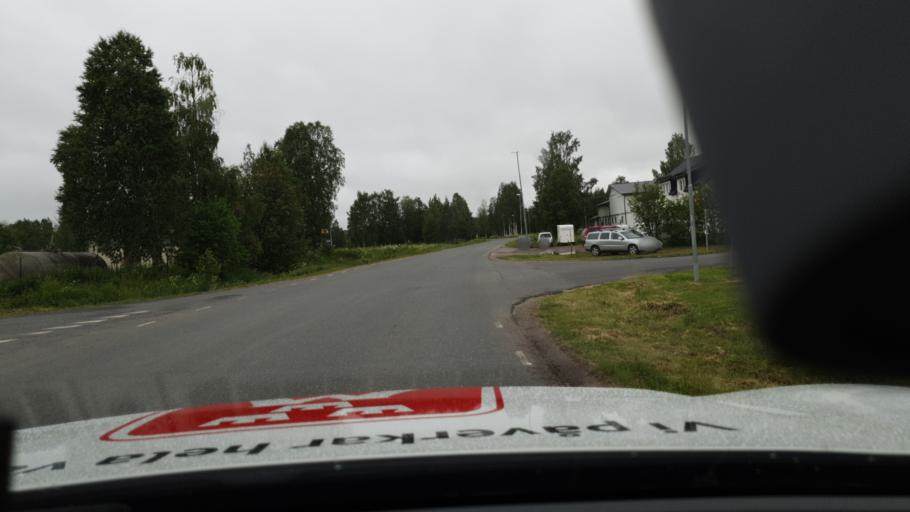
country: SE
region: Norrbotten
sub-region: Overtornea Kommun
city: OEvertornea
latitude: 66.3937
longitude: 23.6357
